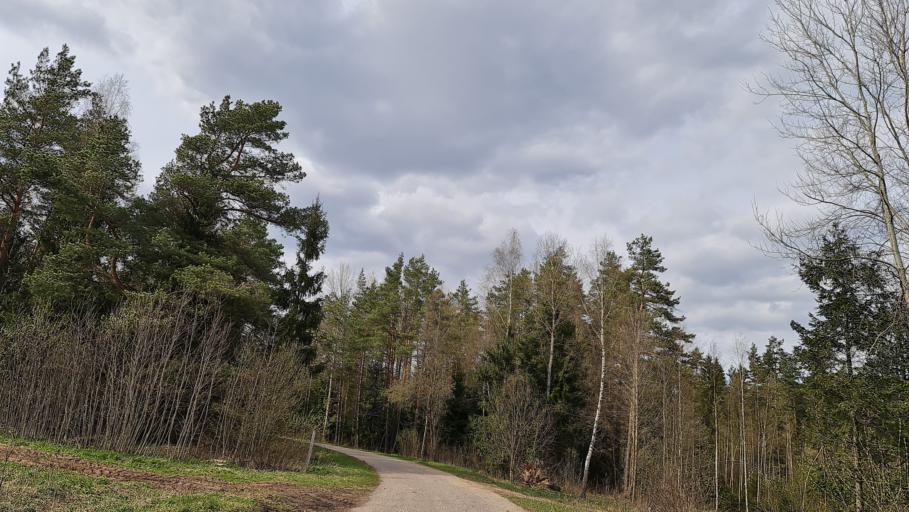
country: BY
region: Vitebsk
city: Byahoml'
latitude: 54.7484
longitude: 28.0409
